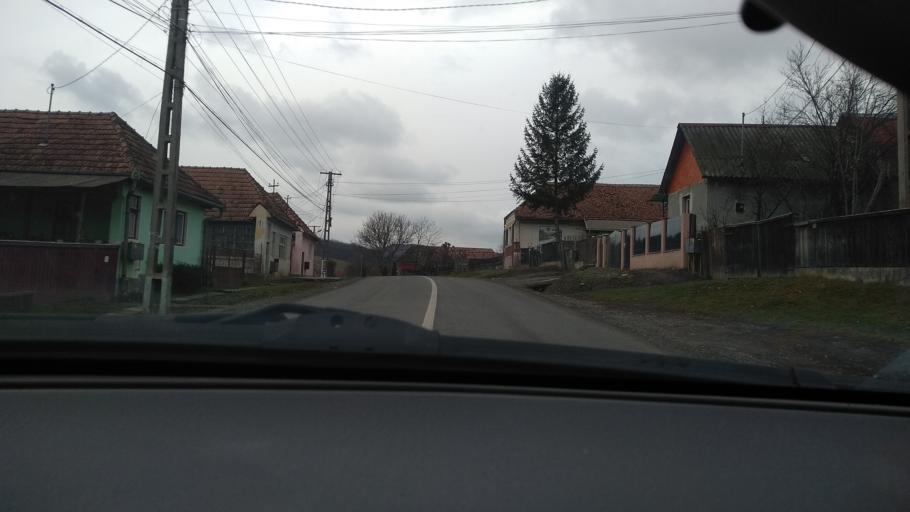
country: RO
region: Mures
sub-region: Comuna Galesti
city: Galesti
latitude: 46.5331
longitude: 24.7652
